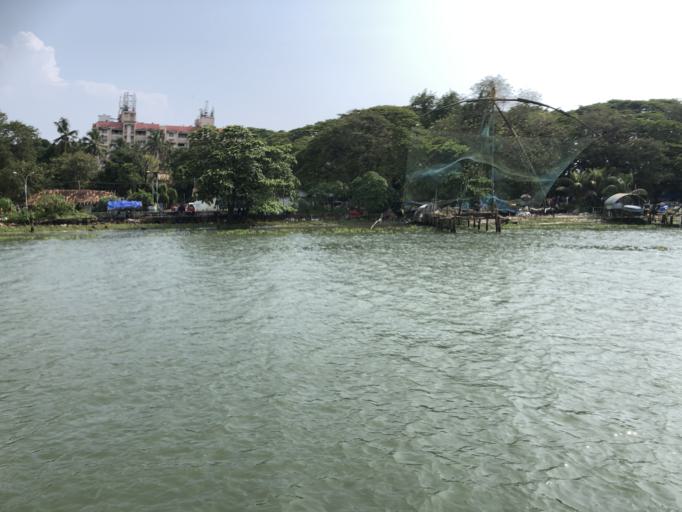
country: IN
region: Kerala
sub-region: Ernakulam
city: Cochin
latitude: 9.9691
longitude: 76.2426
